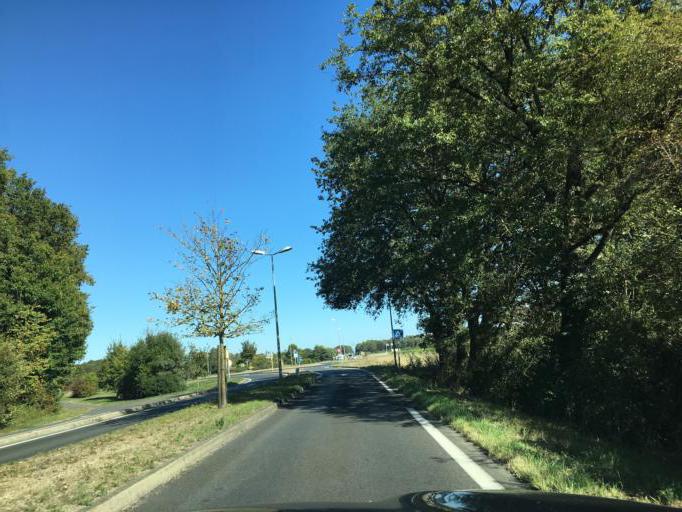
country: FR
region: Centre
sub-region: Departement d'Indre-et-Loire
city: Azay-le-Rideau
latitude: 47.2708
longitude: 0.4814
